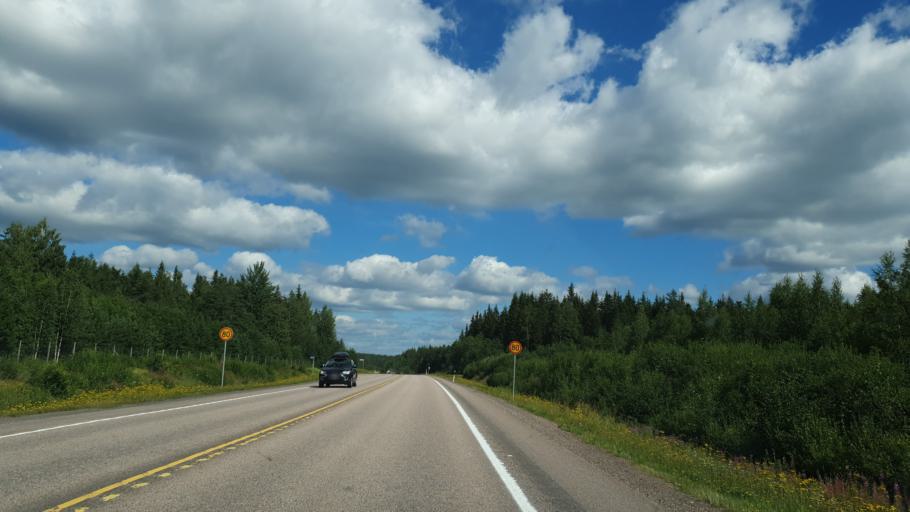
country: FI
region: Central Finland
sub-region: Jaemsae
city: Jaemsae
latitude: 61.8196
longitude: 25.0264
